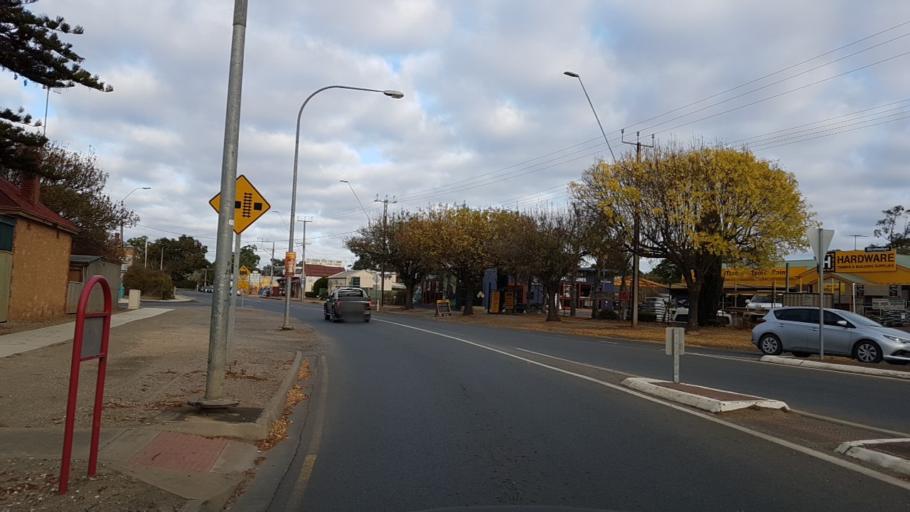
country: AU
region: South Australia
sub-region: Alexandrina
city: Strathalbyn
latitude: -35.2583
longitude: 138.8983
